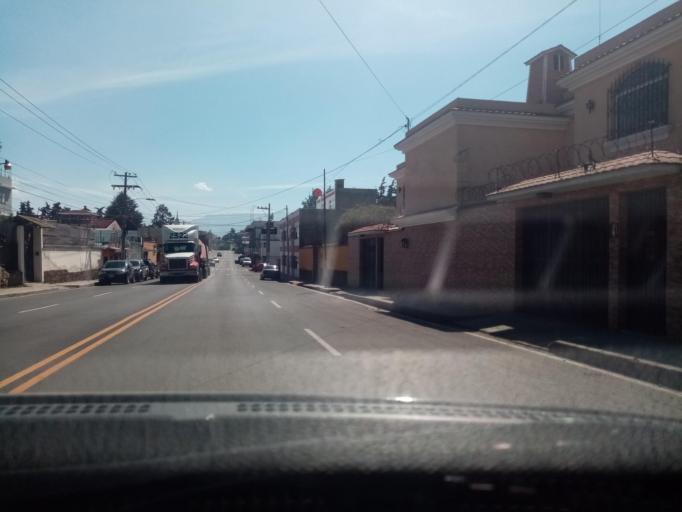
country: GT
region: Quetzaltenango
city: Quetzaltenango
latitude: 14.8465
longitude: -91.5168
